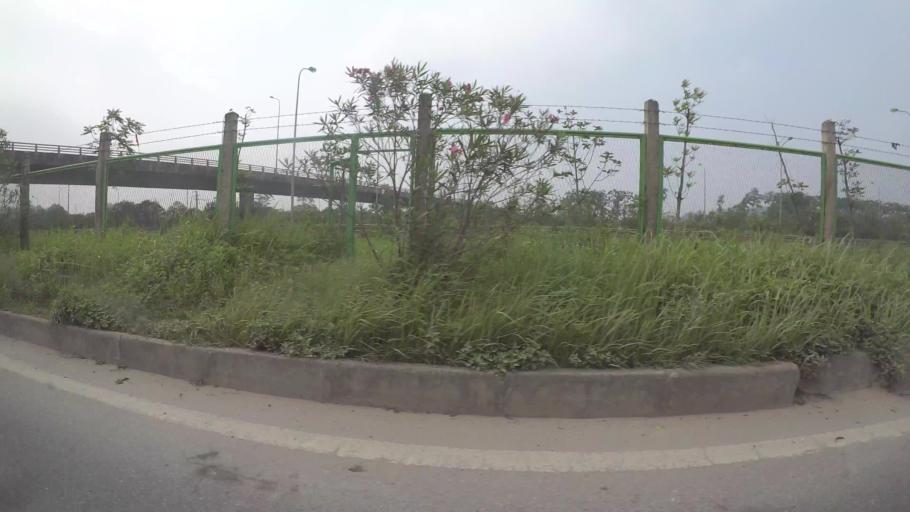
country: VN
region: Ha Noi
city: Quoc Oai
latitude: 21.0037
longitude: 105.6491
